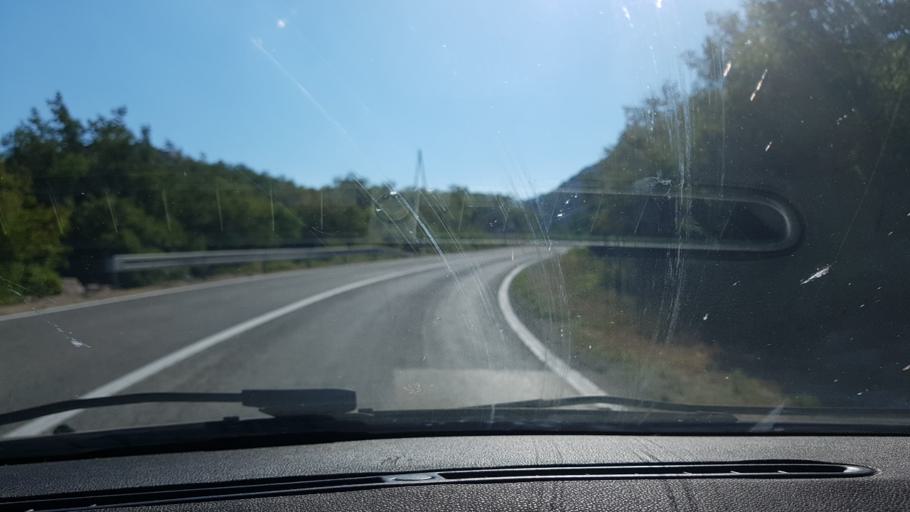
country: HR
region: Zadarska
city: Gracac
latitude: 44.2358
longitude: 15.8165
